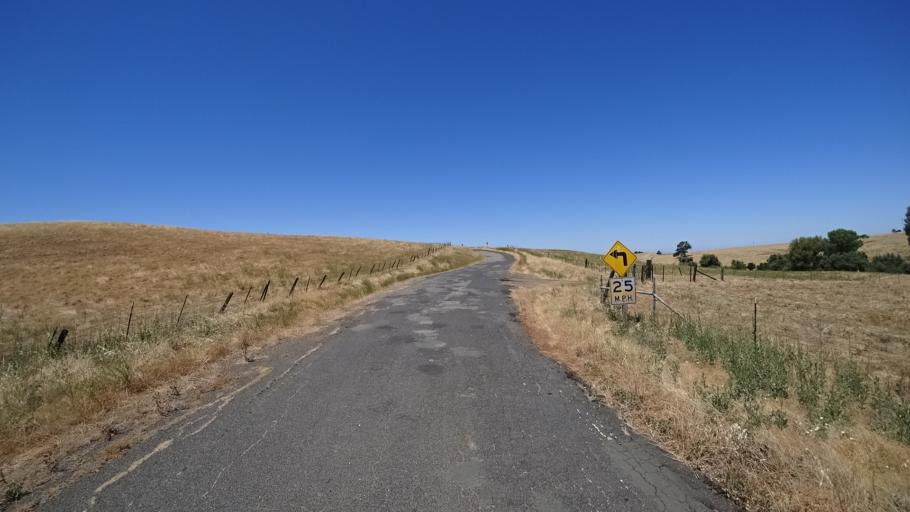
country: US
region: California
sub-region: Calaveras County
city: Rancho Calaveras
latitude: 38.0461
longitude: -120.8325
